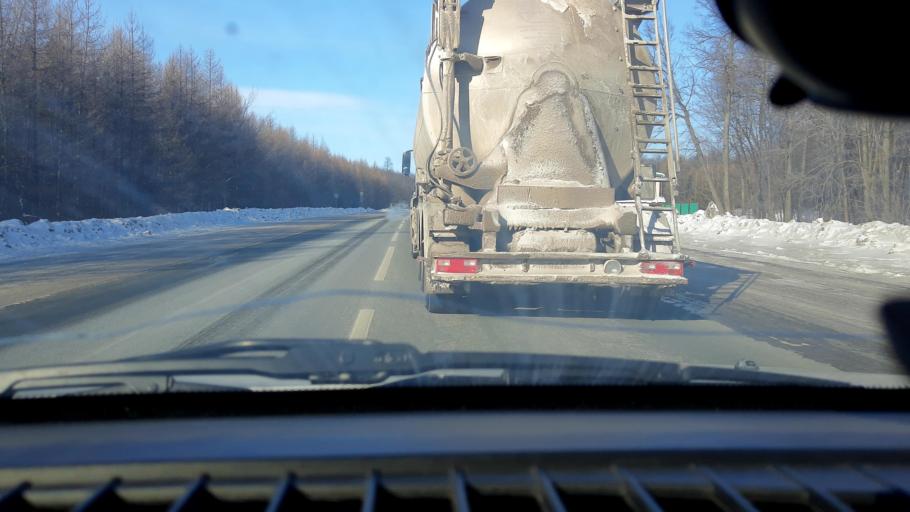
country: RU
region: Bashkortostan
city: Avdon
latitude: 54.7953
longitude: 55.7522
